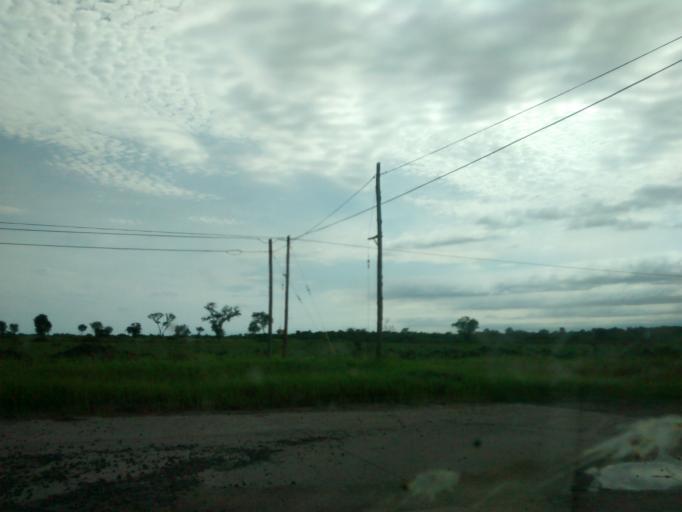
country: AR
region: Chaco
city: Resistencia
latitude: -27.4101
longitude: -58.9613
